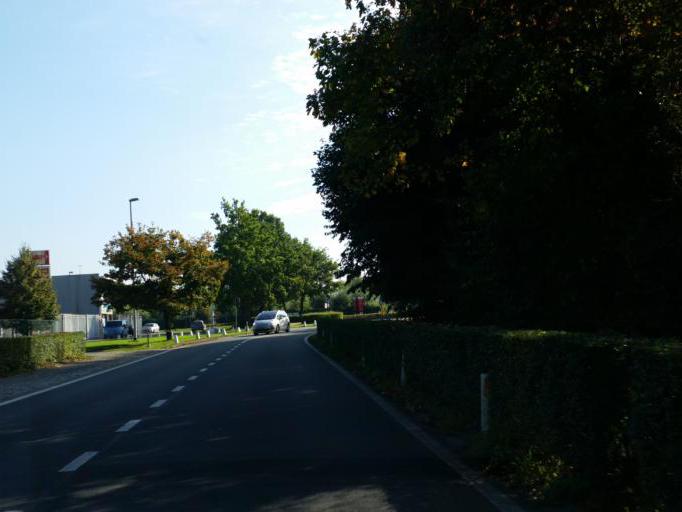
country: BE
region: Flanders
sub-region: Provincie Antwerpen
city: Edegem
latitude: 51.1568
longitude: 4.4159
